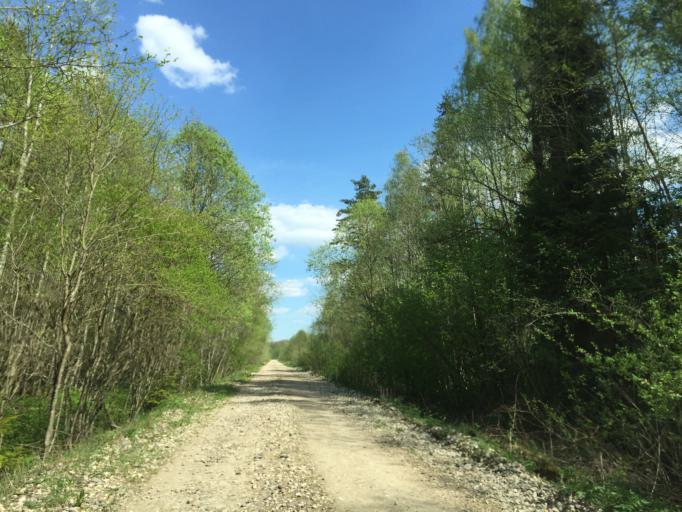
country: LV
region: Limbazu Rajons
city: Limbazi
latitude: 57.4079
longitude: 24.6134
